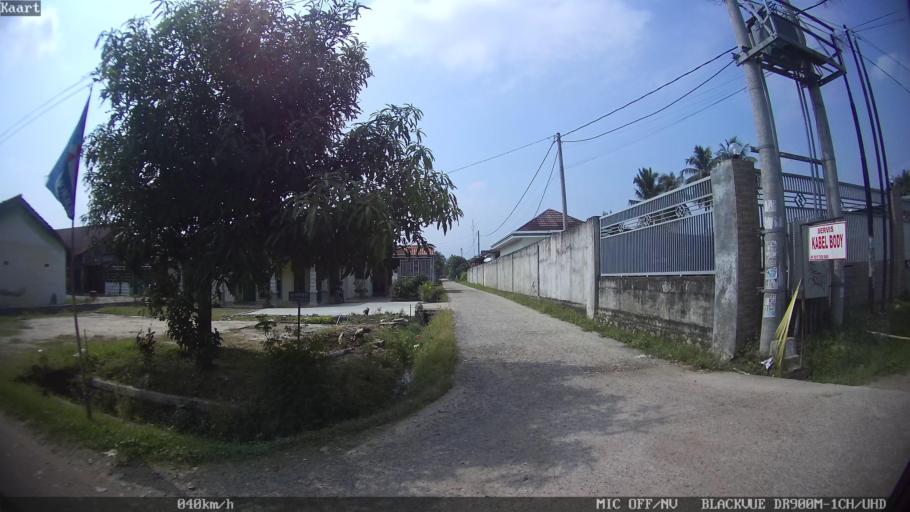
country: ID
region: Lampung
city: Gadingrejo
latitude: -5.3765
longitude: 105.0372
